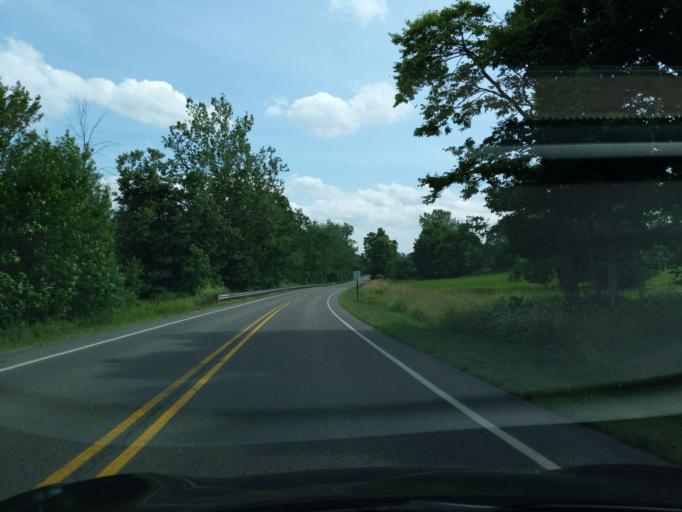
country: US
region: Michigan
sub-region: Eaton County
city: Dimondale
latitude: 42.5897
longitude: -84.6025
